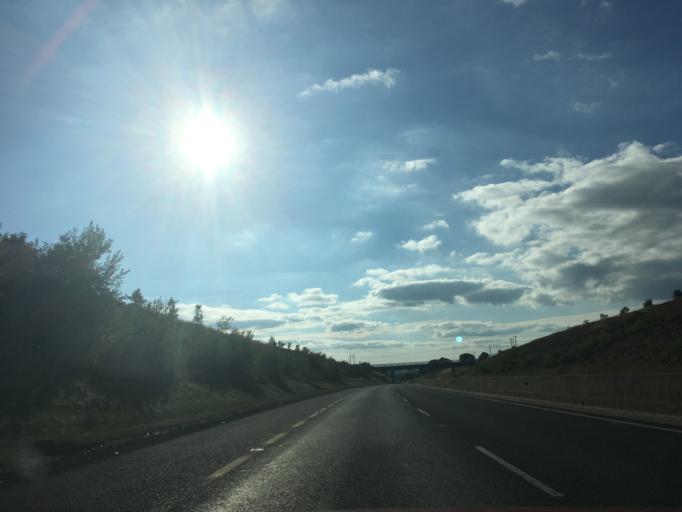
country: IE
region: Munster
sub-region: Waterford
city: Waterford
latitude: 52.2884
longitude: -7.0981
